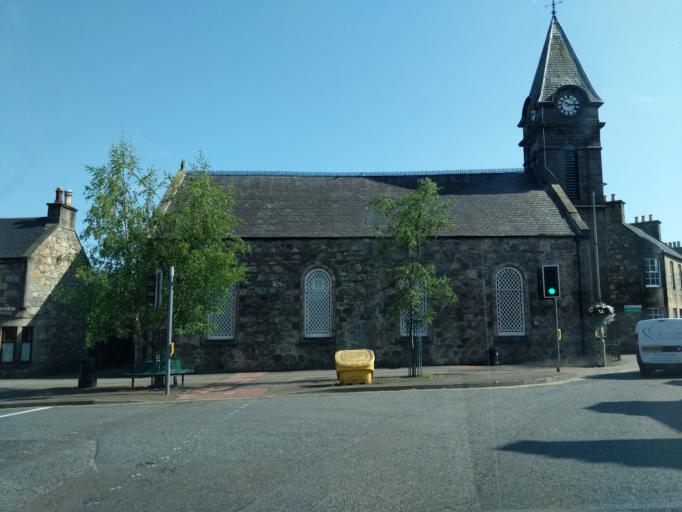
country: GB
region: Scotland
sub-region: Moray
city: Rothes
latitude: 57.5272
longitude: -3.2078
